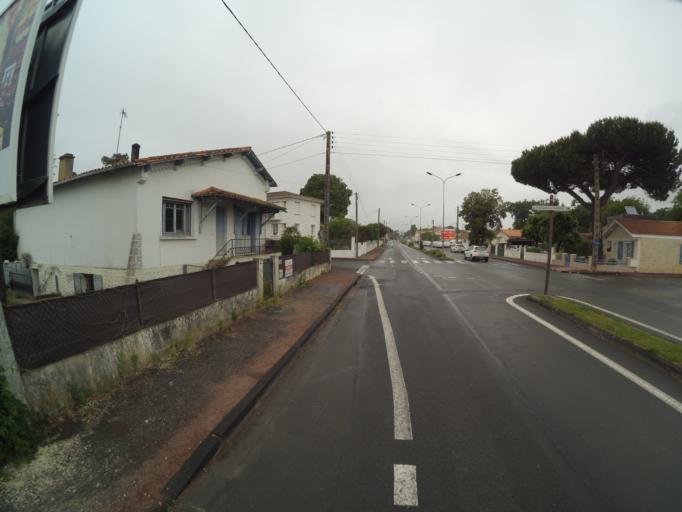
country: FR
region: Poitou-Charentes
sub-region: Departement de la Charente-Maritime
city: Saint-Georges-de-Didonne
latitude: 45.6145
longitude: -1.0007
